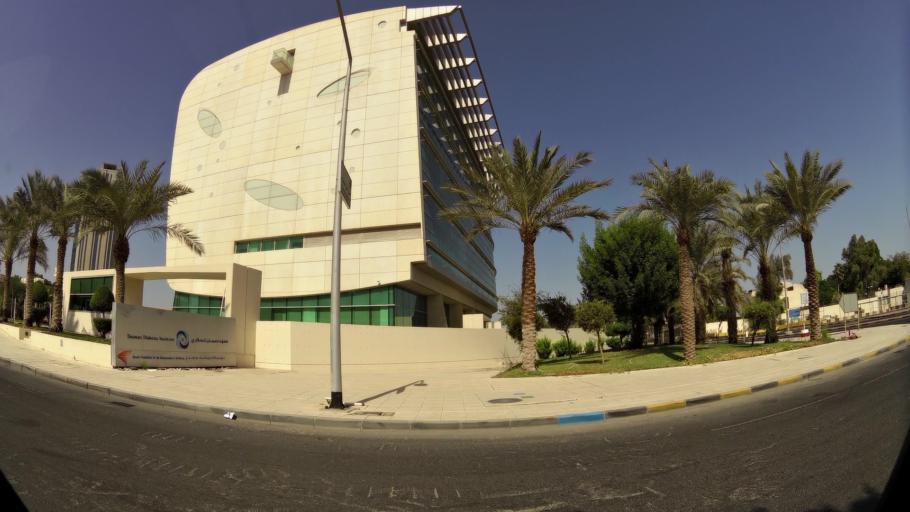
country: KW
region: Al Asimah
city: Kuwait City
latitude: 29.3890
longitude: 47.9942
